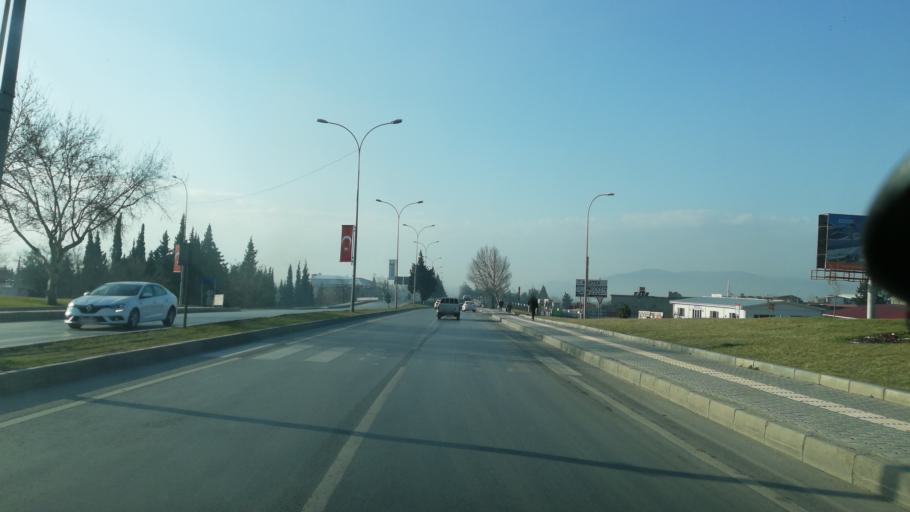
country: TR
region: Kahramanmaras
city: Kahramanmaras
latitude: 37.5677
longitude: 36.9246
